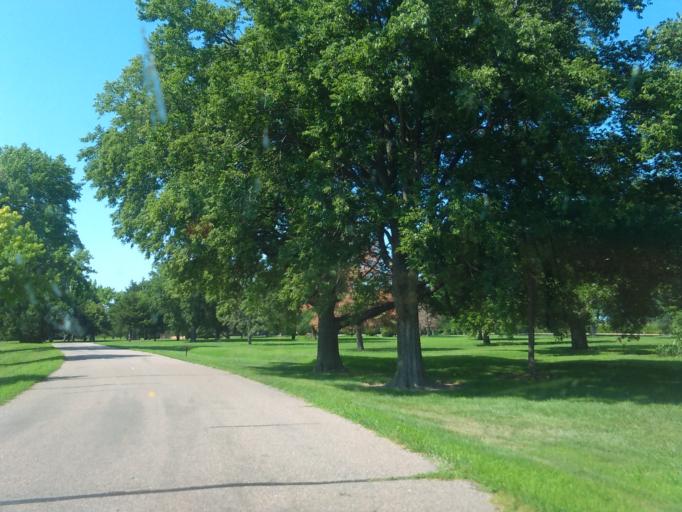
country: US
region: Nebraska
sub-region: Buffalo County
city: Kearney
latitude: 40.6414
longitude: -99.0049
